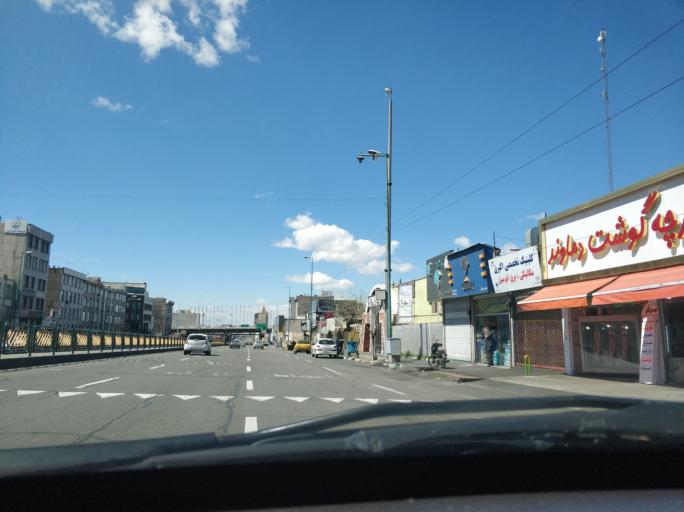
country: IR
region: Tehran
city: Tehran
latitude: 35.7193
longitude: 51.5051
